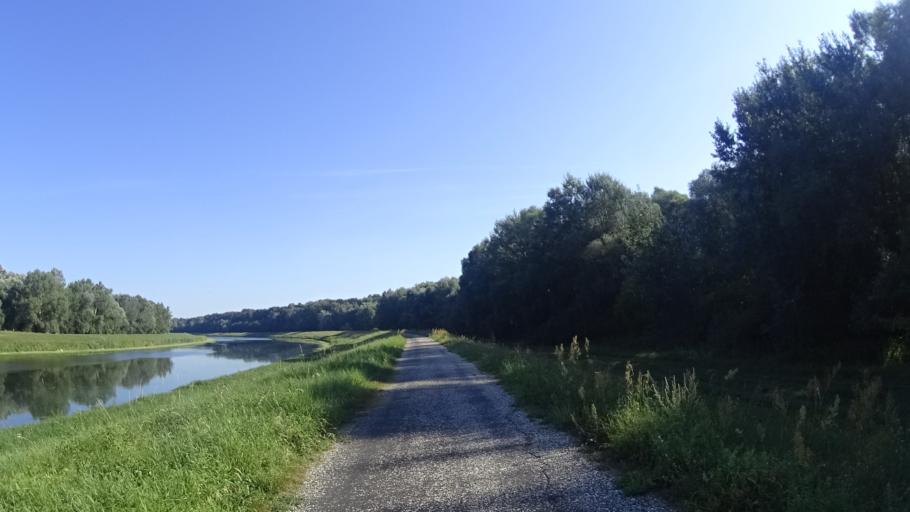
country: CZ
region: South Moravian
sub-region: Okres Breclav
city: Lanzhot
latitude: 48.6916
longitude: 16.9981
